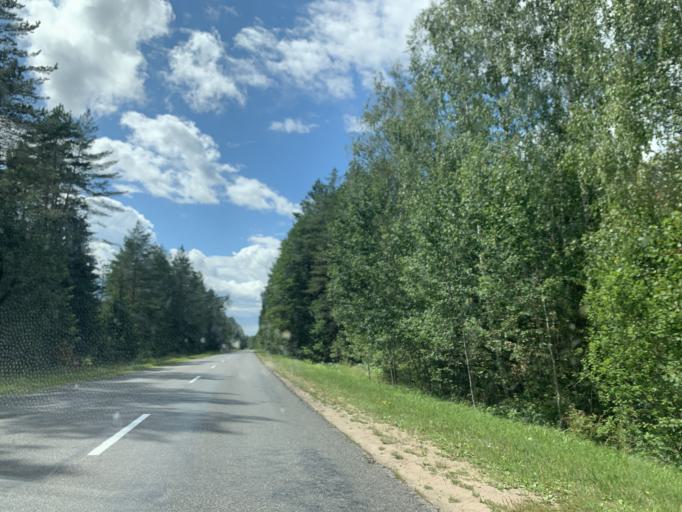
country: BY
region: Minsk
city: Rakaw
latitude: 53.9863
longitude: 26.9324
